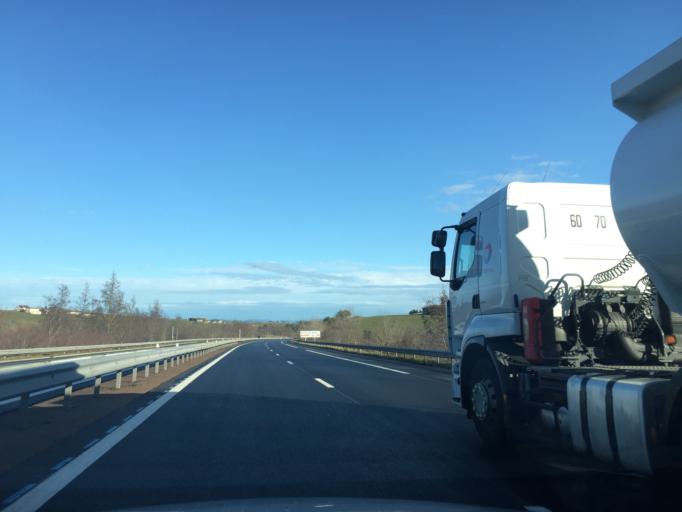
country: FR
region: Rhone-Alpes
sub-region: Departement de la Loire
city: Saint-Germain-Laval
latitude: 45.8615
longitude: 3.9951
